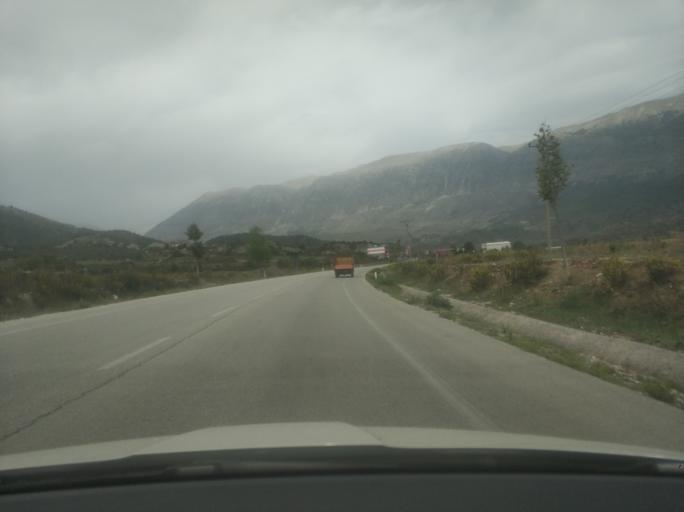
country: AL
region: Gjirokaster
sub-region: Rrethi i Gjirokastres
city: Picar
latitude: 40.1838
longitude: 20.0765
